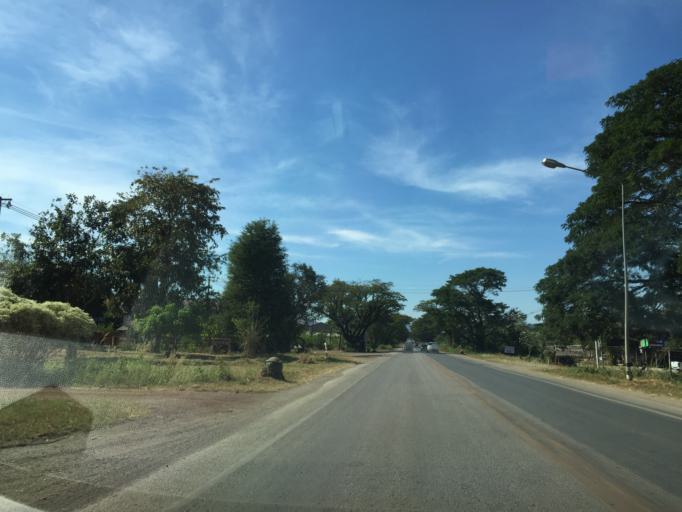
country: TH
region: Changwat Nong Bua Lamphu
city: Na Wang
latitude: 17.3214
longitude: 102.0947
